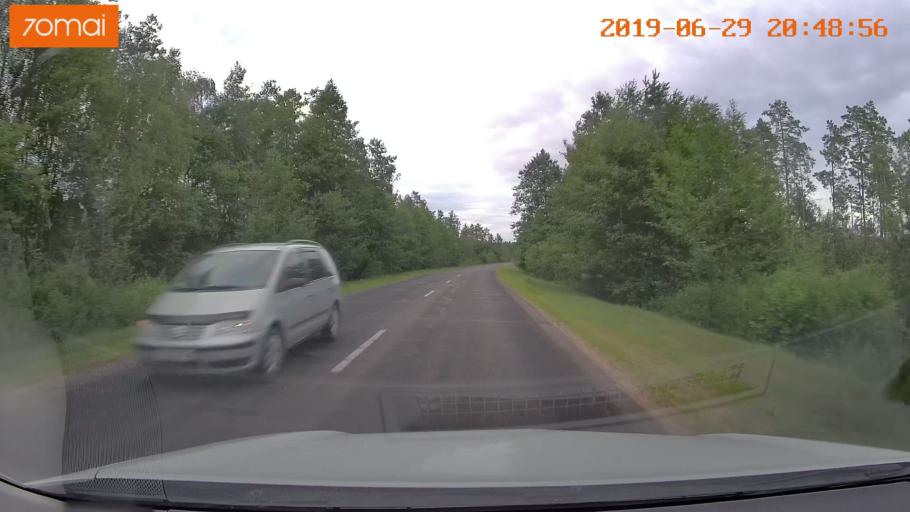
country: BY
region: Brest
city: Hantsavichy
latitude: 52.6580
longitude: 26.3189
